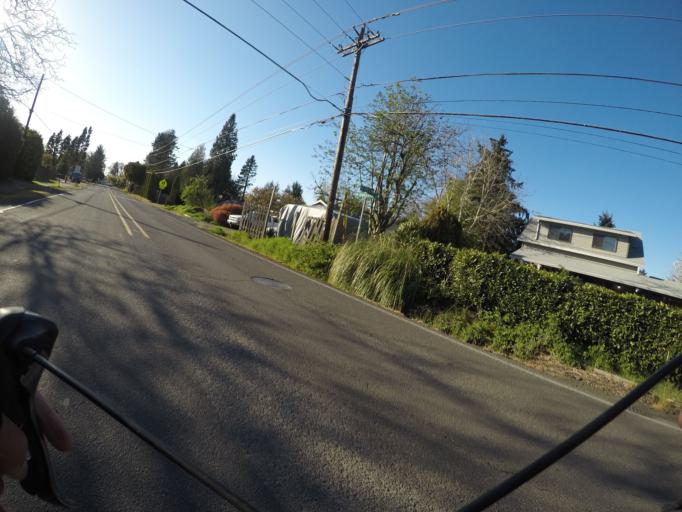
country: US
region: Oregon
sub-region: Washington County
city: Aloha
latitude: 45.4877
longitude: -122.8738
